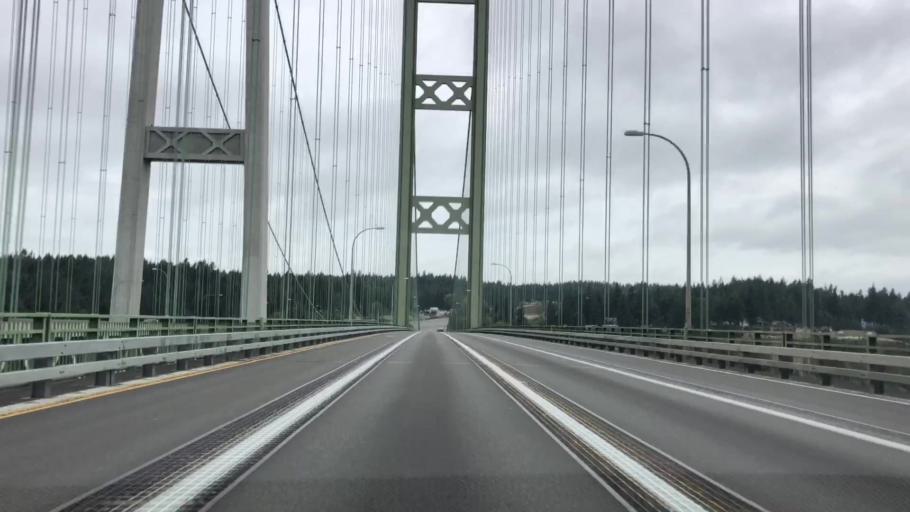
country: US
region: Washington
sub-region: Pierce County
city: Wollochet
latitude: 47.2698
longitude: -122.5523
